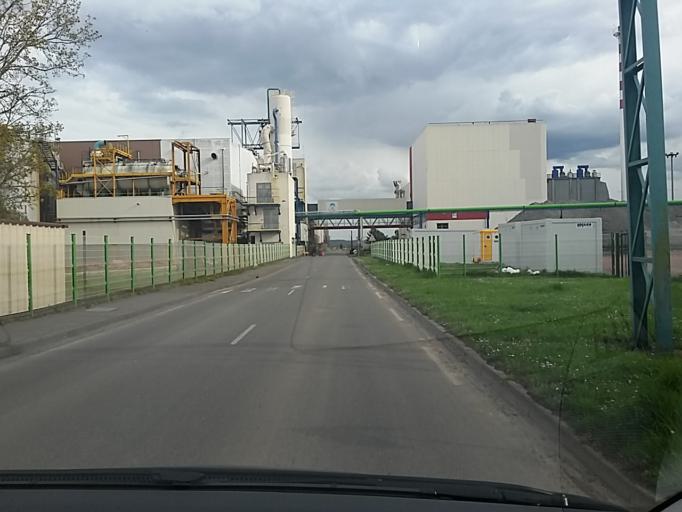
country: FR
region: Picardie
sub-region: Departement de l'Oise
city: Grandfresnoy
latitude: 49.3615
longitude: 2.6651
